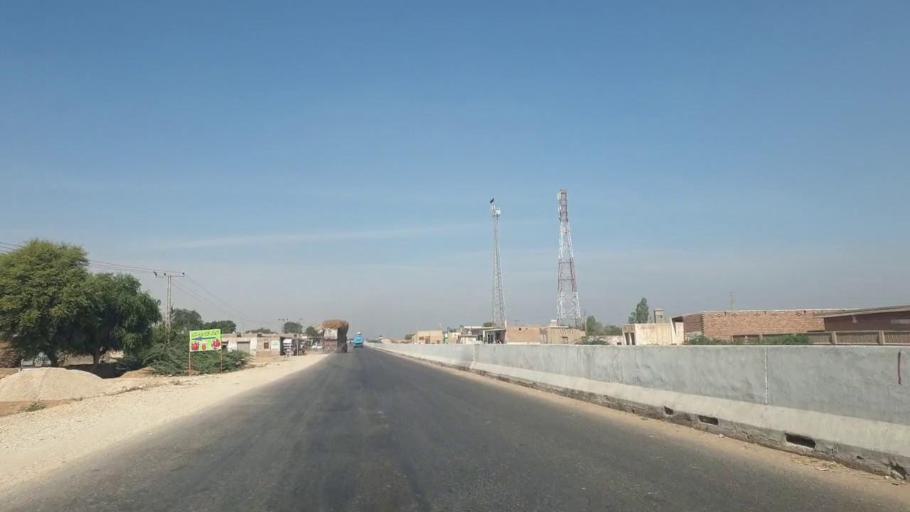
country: PK
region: Sindh
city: Matiari
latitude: 25.6480
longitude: 68.3010
